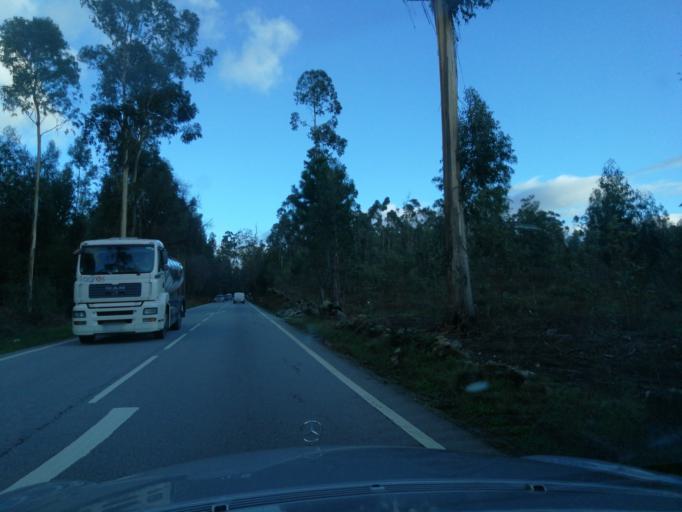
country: PT
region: Braga
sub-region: Esposende
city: Marinhas
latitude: 41.5801
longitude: -8.7285
